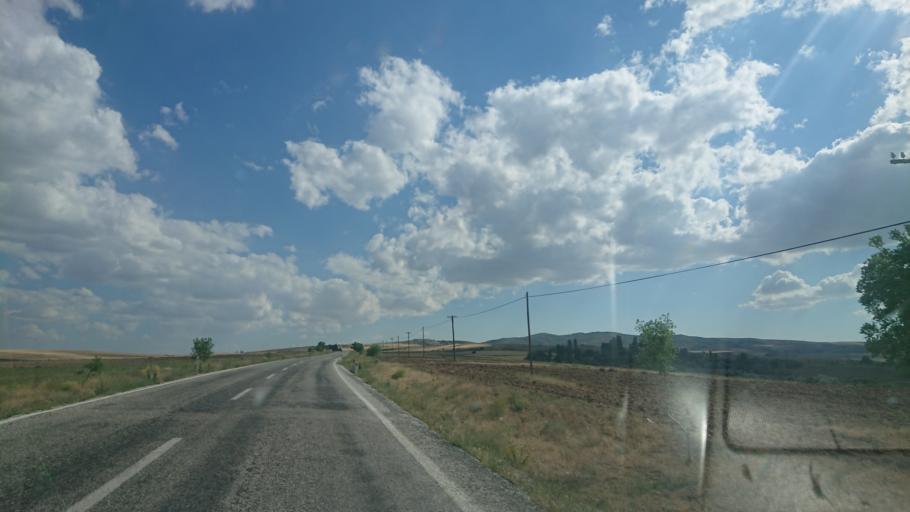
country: TR
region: Aksaray
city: Sariyahsi
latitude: 38.9478
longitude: 33.8385
